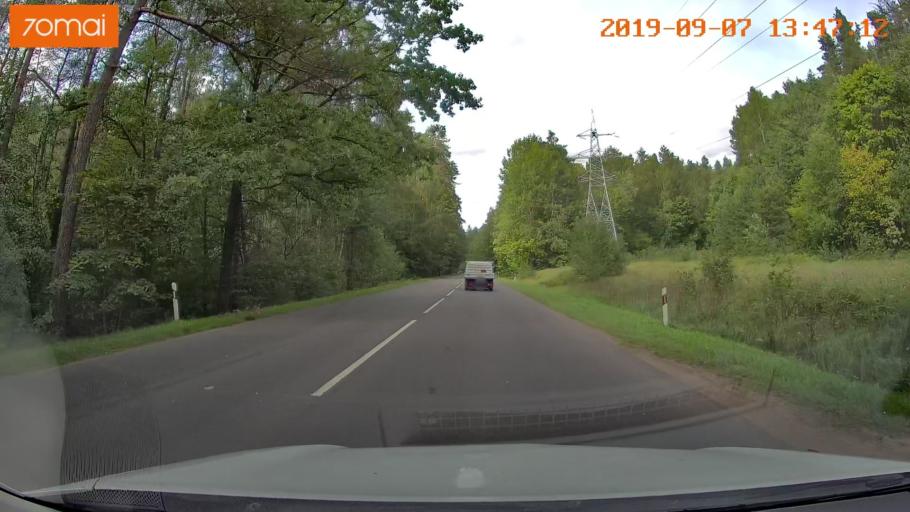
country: LT
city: Baltoji Voke
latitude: 54.5955
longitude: 25.2174
